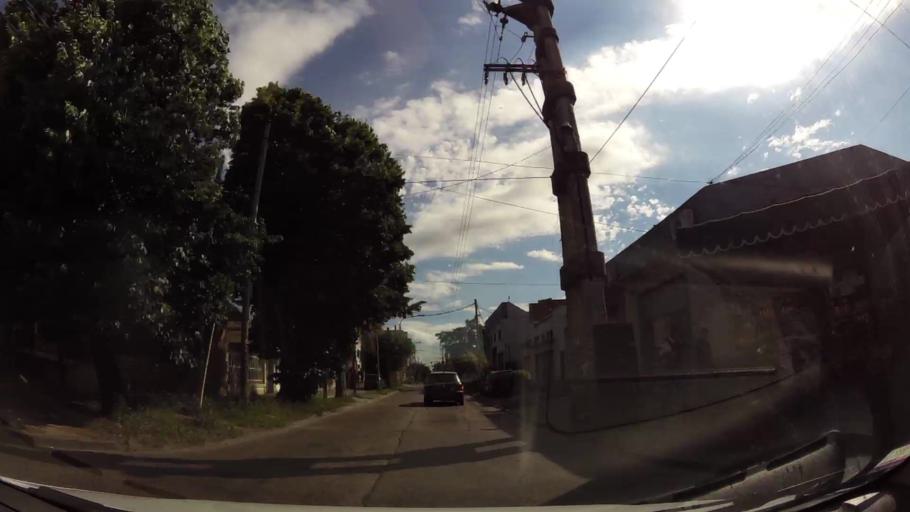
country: AR
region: Buenos Aires
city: San Justo
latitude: -34.6566
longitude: -58.5805
